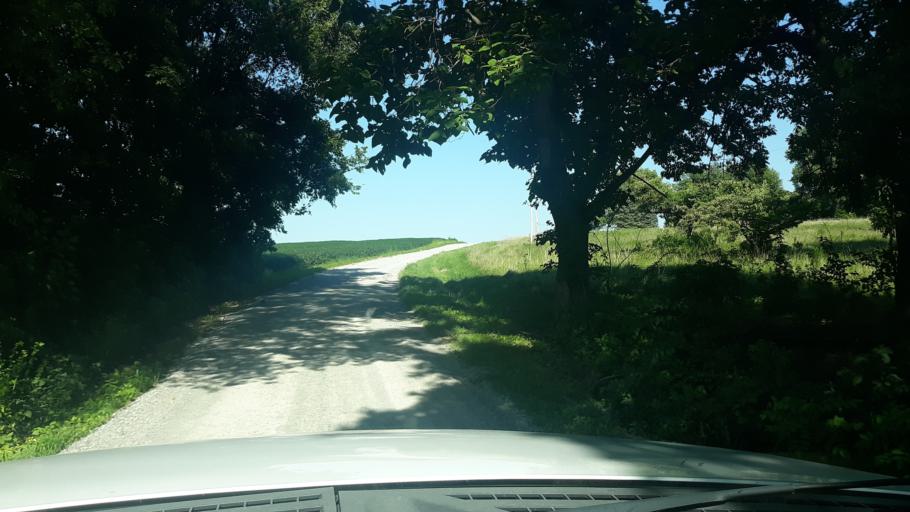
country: US
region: Illinois
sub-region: Saline County
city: Eldorado
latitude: 37.8466
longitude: -88.4905
